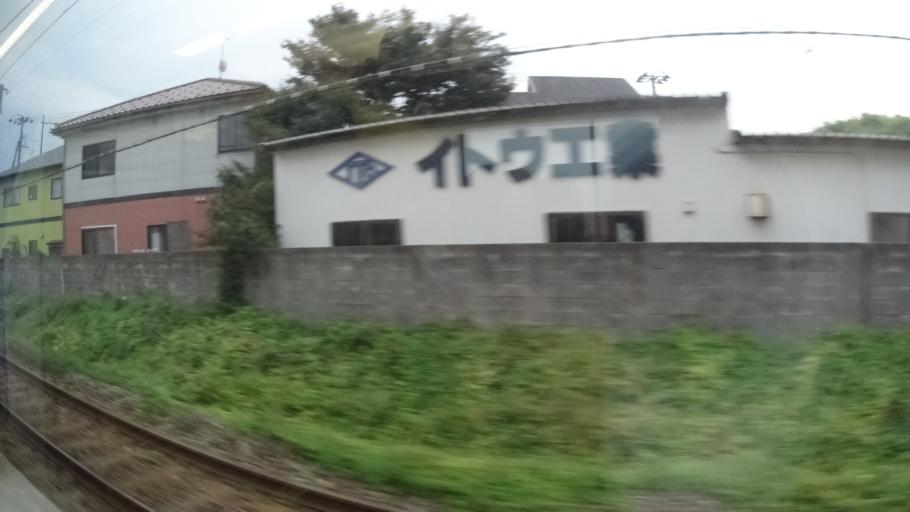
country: JP
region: Niigata
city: Murakami
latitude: 38.2271
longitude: 139.4624
